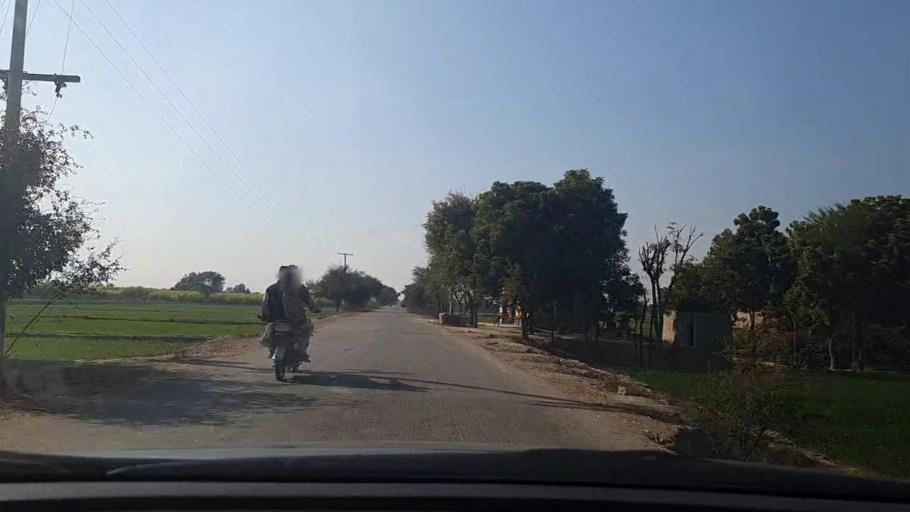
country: PK
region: Sindh
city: Daulatpur
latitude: 26.3197
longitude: 68.0452
